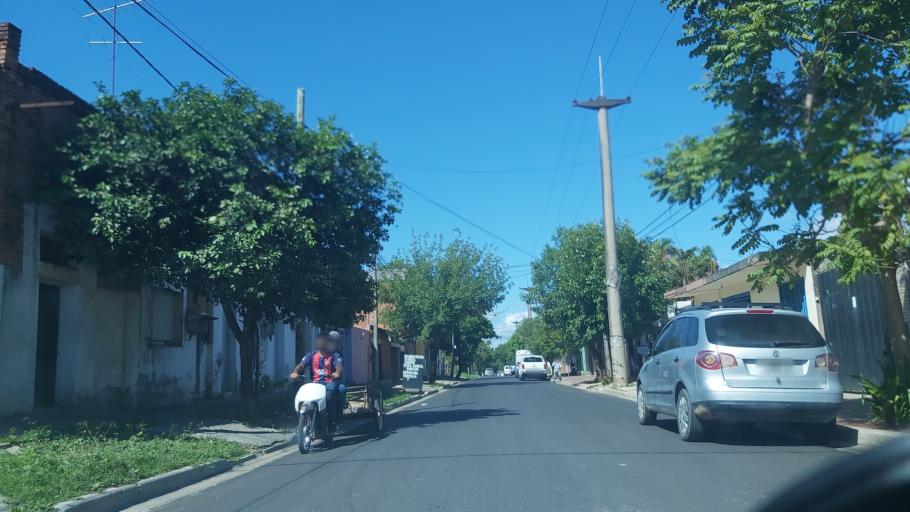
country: AR
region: Corrientes
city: Corrientes
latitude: -27.4805
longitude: -58.8477
